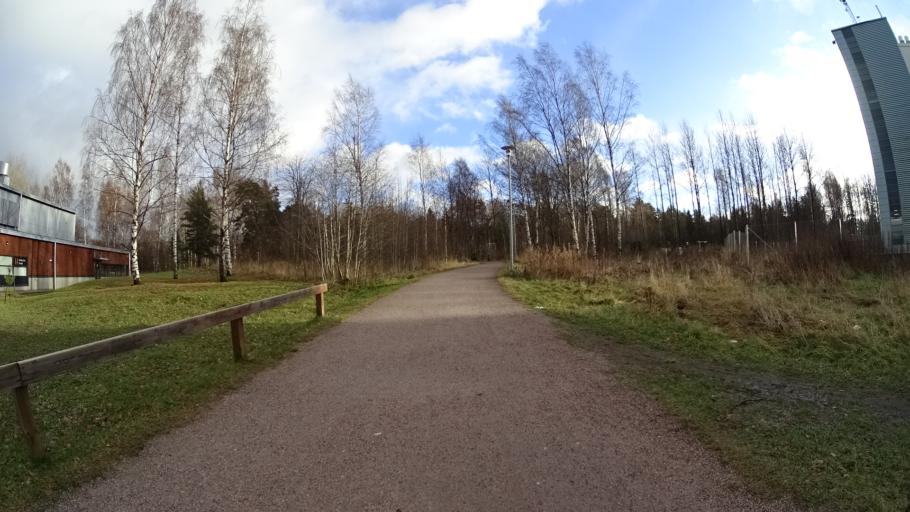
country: FI
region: Uusimaa
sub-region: Helsinki
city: Koukkuniemi
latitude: 60.1784
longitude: 24.7868
